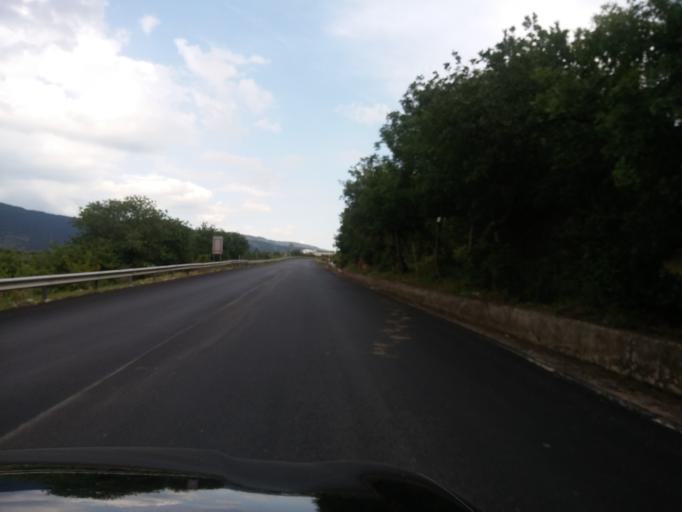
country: IT
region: Apulia
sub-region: Provincia di Foggia
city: Rignano Garganico
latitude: 41.7141
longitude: 15.5469
